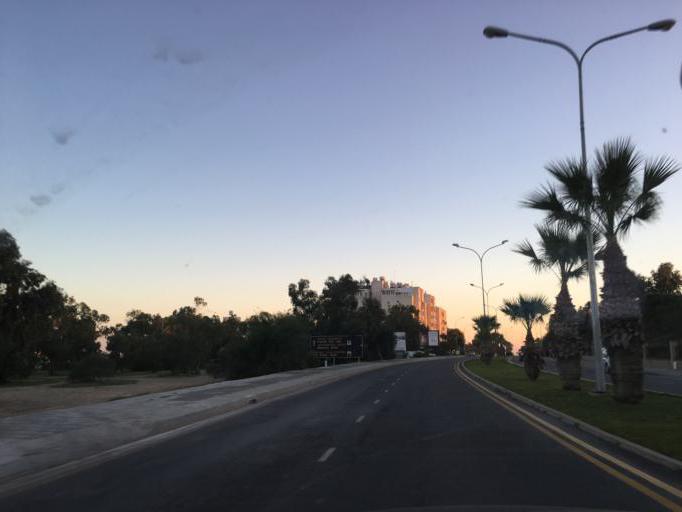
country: CY
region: Larnaka
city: Larnaca
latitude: 34.9038
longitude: 33.6303
